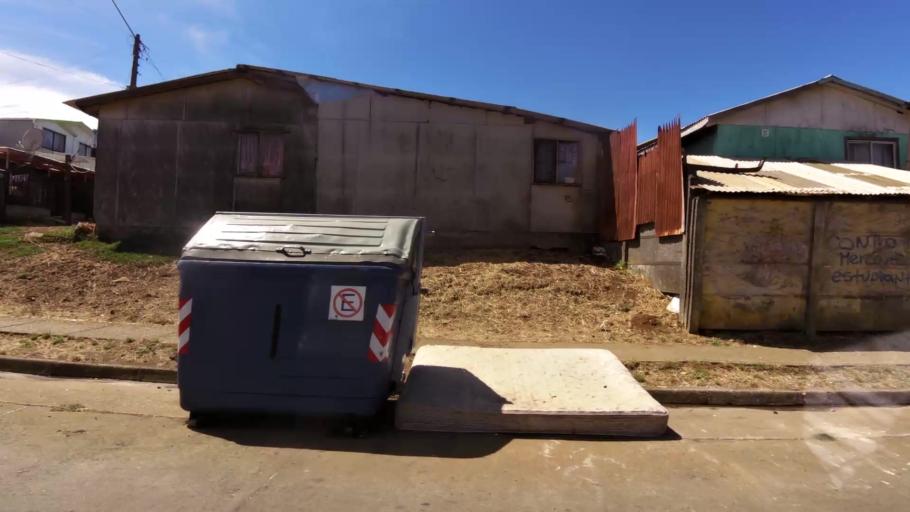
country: CL
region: Biobio
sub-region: Provincia de Concepcion
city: Talcahuano
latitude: -36.7138
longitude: -73.1404
